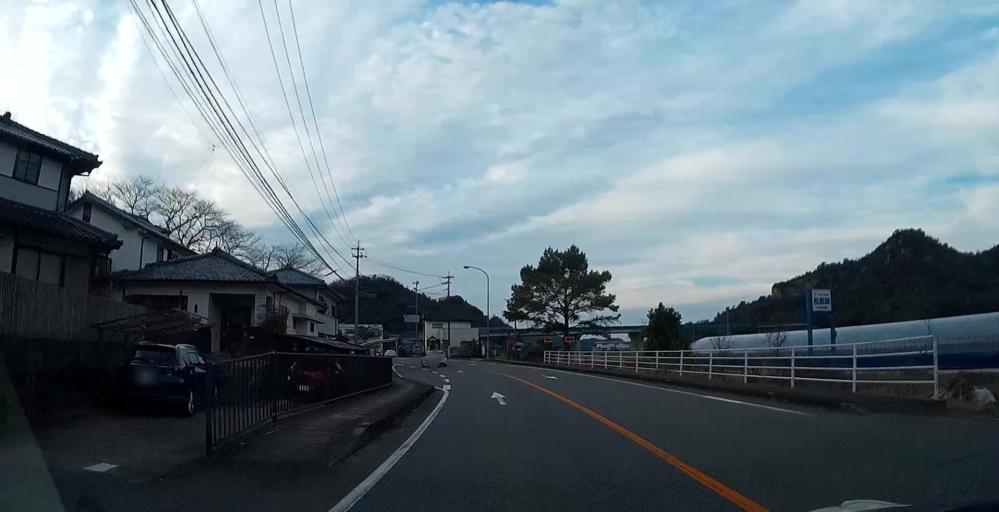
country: JP
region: Kumamoto
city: Yatsushiro
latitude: 32.5000
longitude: 130.4023
